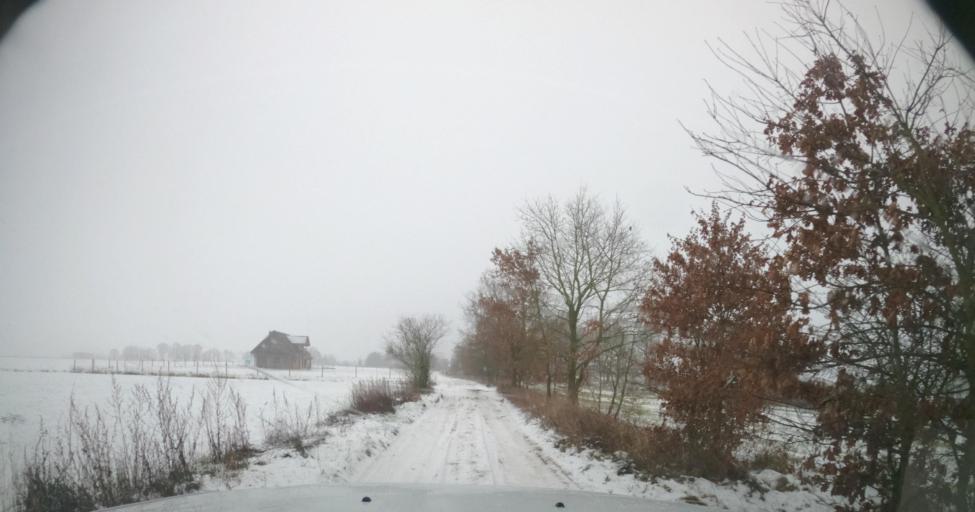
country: PL
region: West Pomeranian Voivodeship
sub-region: Powiat kamienski
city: Golczewo
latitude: 53.8694
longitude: 15.0646
